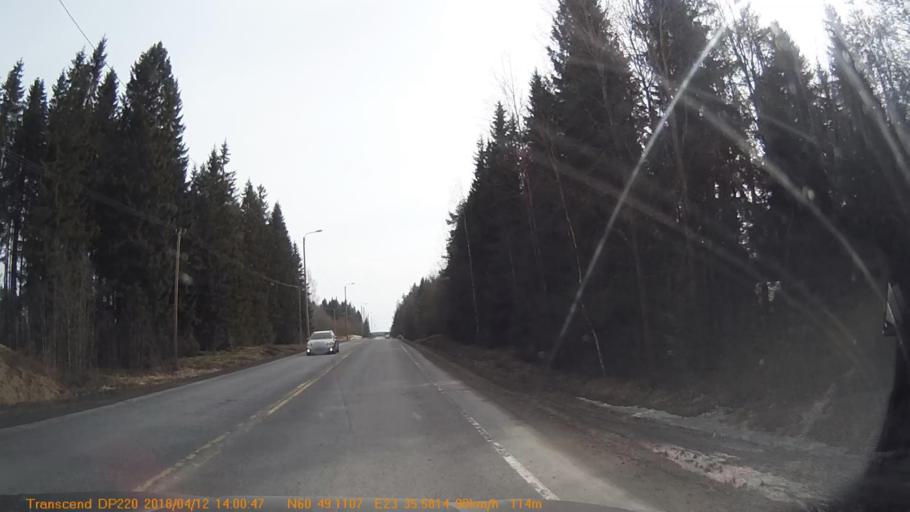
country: FI
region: Haeme
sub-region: Forssa
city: Forssa
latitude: 60.8183
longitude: 23.5932
